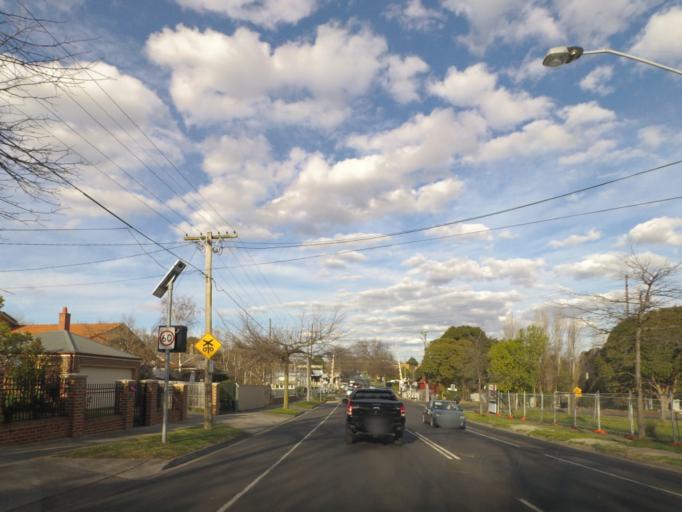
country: AU
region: Victoria
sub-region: Whitehorse
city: Surrey Hills
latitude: -37.8209
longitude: 145.1024
